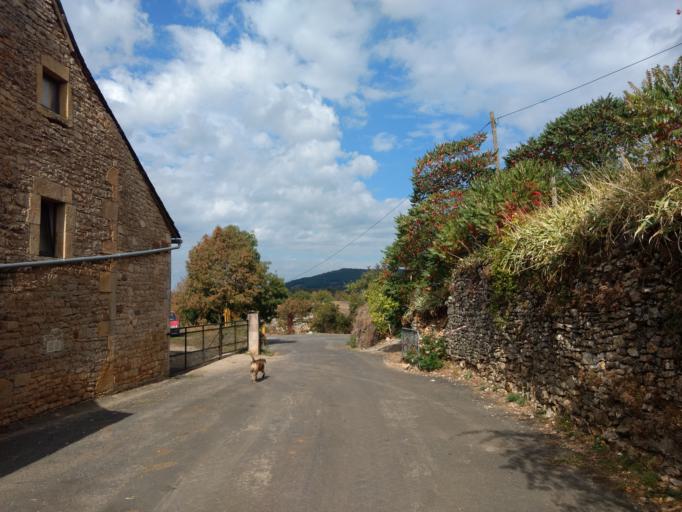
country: FR
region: Midi-Pyrenees
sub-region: Departement de l'Aveyron
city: Bozouls
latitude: 44.4685
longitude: 2.7150
